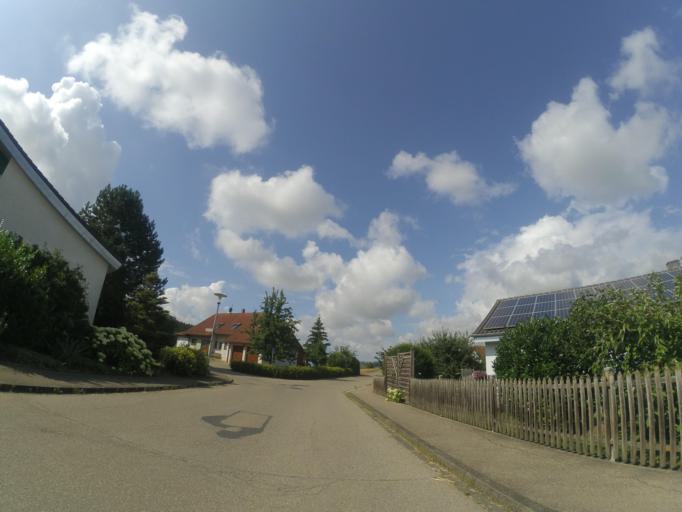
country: DE
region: Baden-Wuerttemberg
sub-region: Tuebingen Region
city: Bernstadt
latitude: 48.4946
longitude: 10.0251
